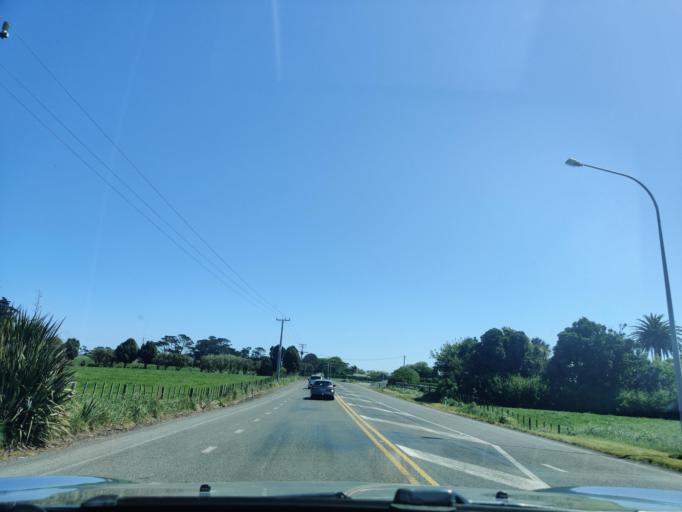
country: NZ
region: Taranaki
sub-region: South Taranaki District
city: Hawera
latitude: -39.6024
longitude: 174.3084
